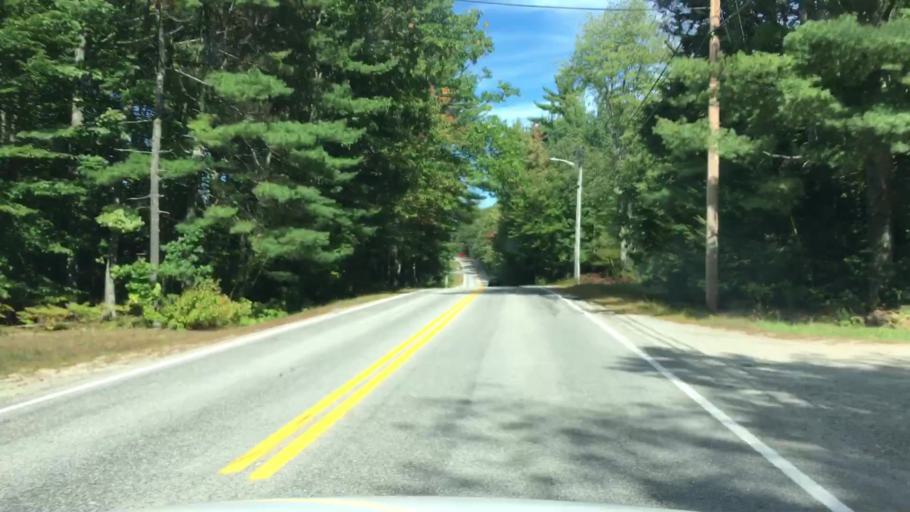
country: US
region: Maine
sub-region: Cumberland County
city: West Scarborough
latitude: 43.5994
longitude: -70.4257
